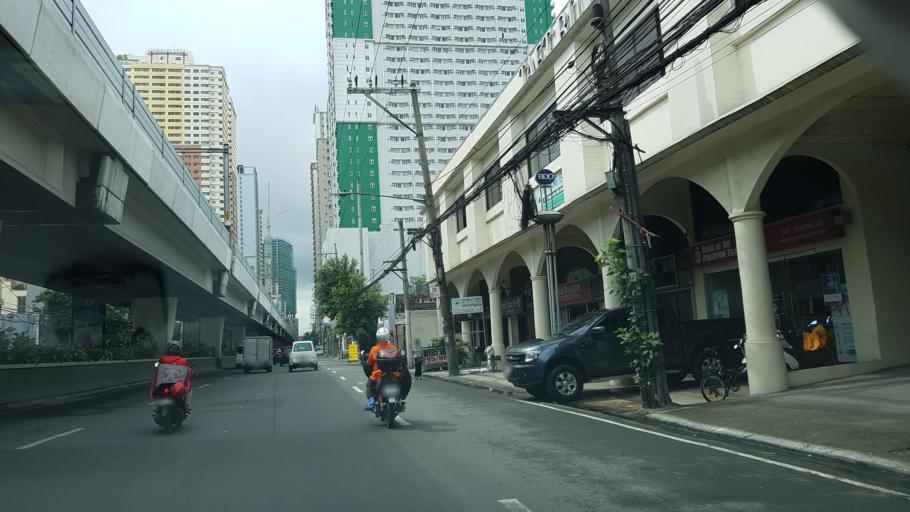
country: PH
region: Metro Manila
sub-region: City of Manila
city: Port Area
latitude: 14.5693
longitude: 120.9920
